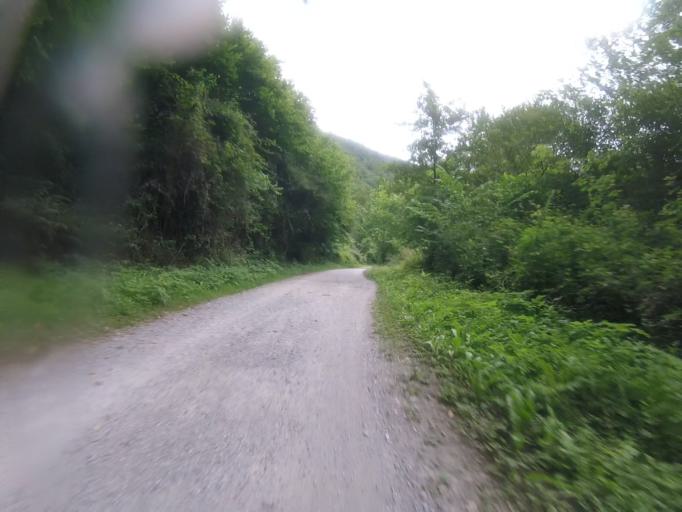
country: ES
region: Navarre
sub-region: Provincia de Navarra
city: Sunbilla
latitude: 43.2007
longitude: -1.6738
